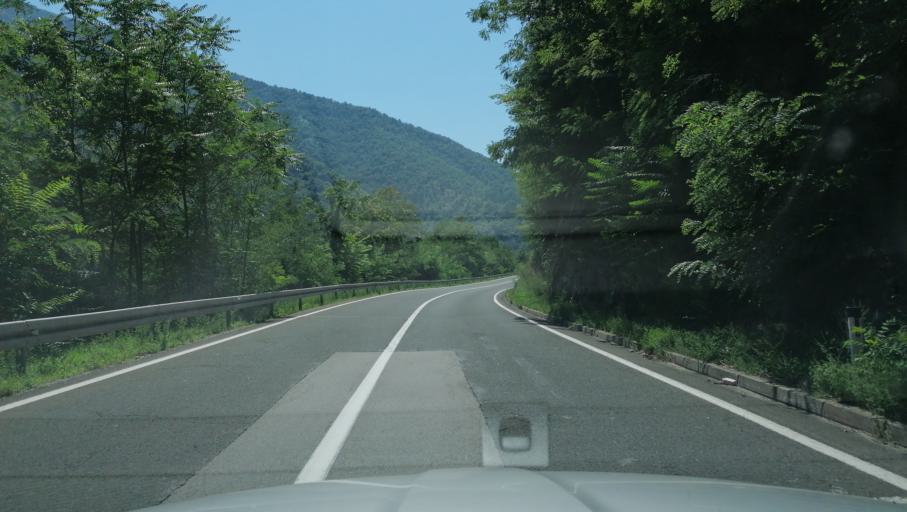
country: RS
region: Central Serbia
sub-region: Raski Okrug
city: Kraljevo
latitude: 43.6411
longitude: 20.5516
